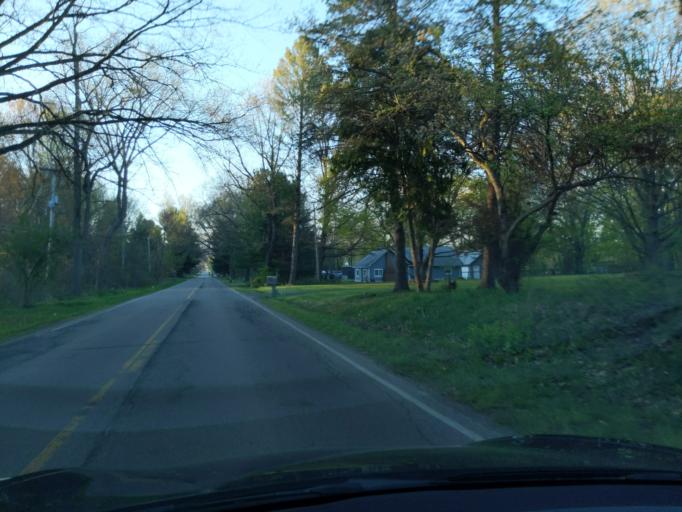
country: US
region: Michigan
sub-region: Jackson County
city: Jackson
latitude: 42.2624
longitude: -84.4832
